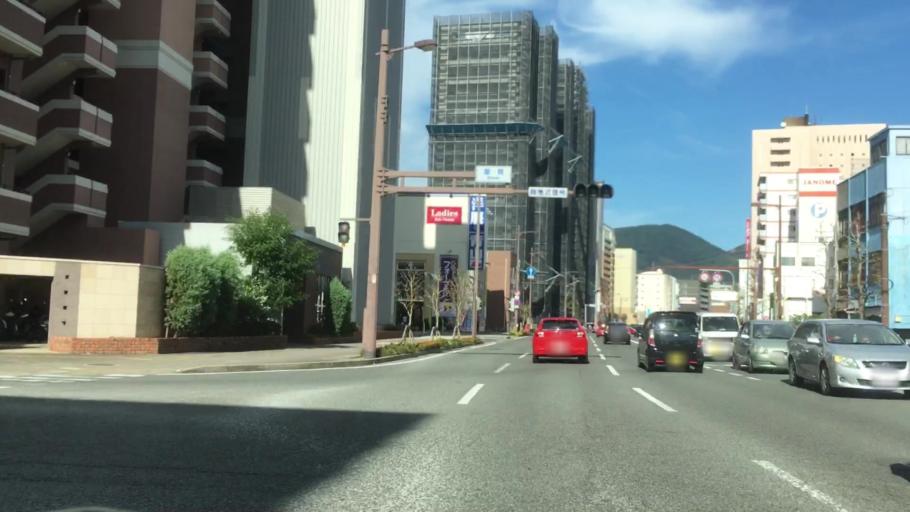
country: JP
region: Nagasaki
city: Sasebo
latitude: 33.1623
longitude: 129.7292
